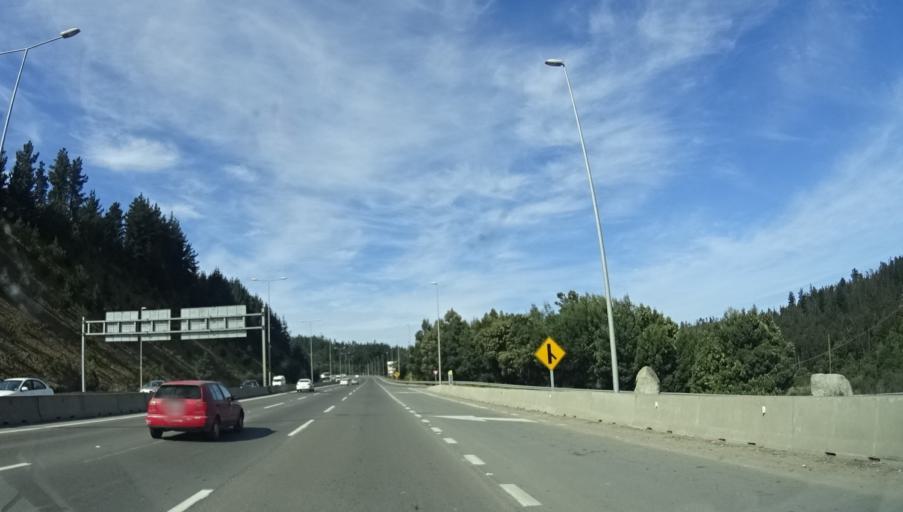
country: CL
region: Valparaiso
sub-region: Provincia de Valparaiso
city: Vina del Mar
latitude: -33.1083
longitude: -71.5543
